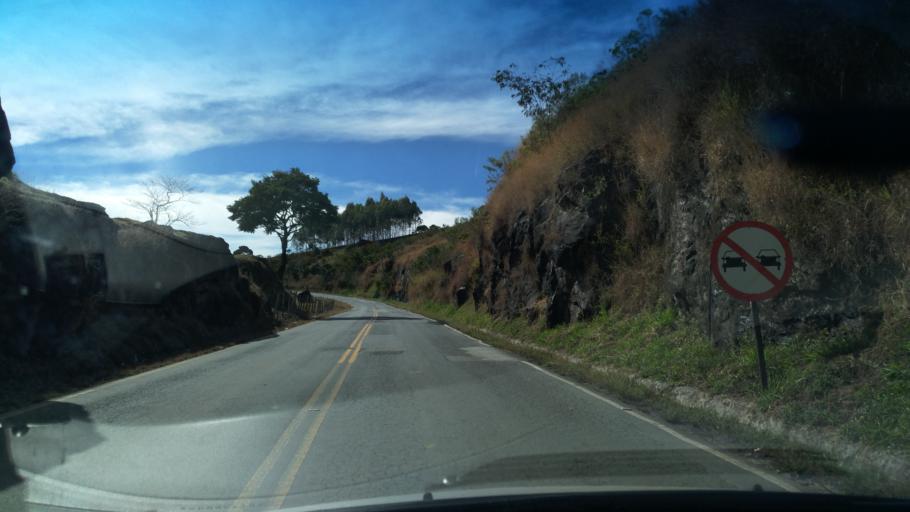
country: BR
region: Minas Gerais
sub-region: Andradas
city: Andradas
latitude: -22.0529
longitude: -46.3625
